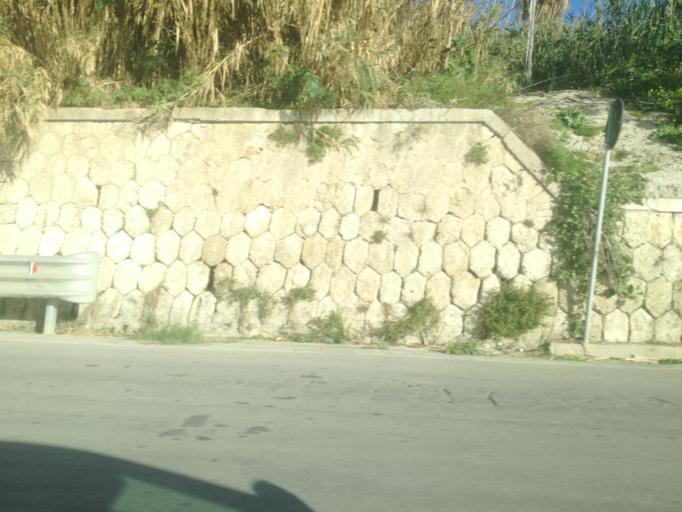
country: IT
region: Sicily
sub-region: Provincia di Caltanissetta
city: Gela
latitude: 37.0671
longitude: 14.2365
